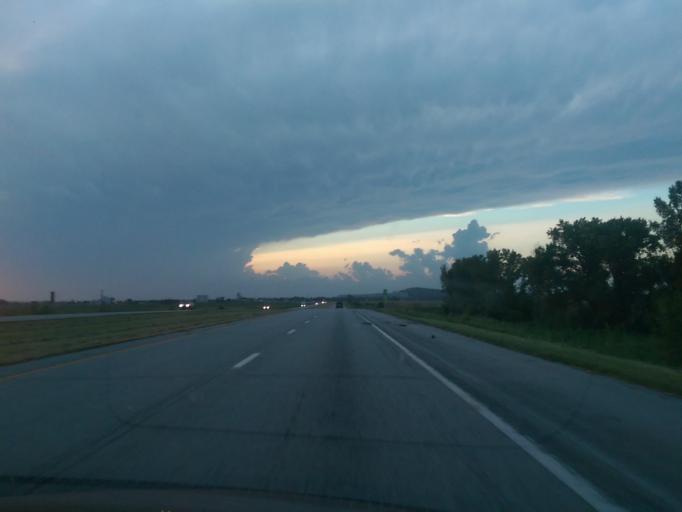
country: US
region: Iowa
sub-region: Fremont County
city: Hamburg
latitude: 40.5719
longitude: -95.6432
